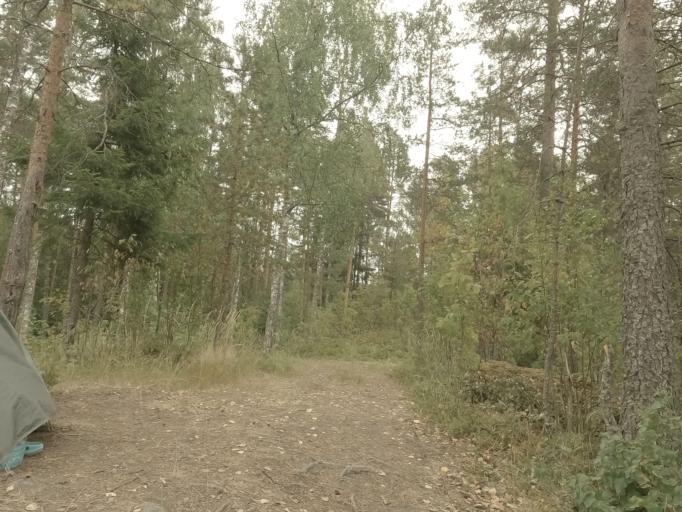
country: RU
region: Leningrad
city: Kamennogorsk
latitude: 61.0783
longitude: 29.1552
